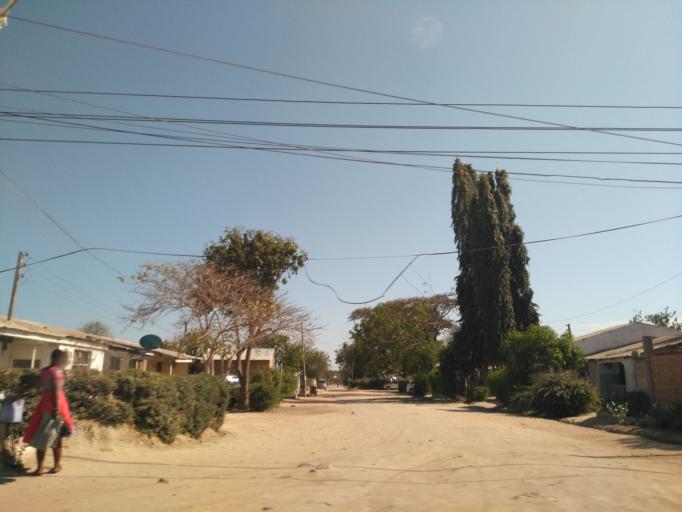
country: TZ
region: Dodoma
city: Dodoma
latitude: -6.1636
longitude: 35.7477
